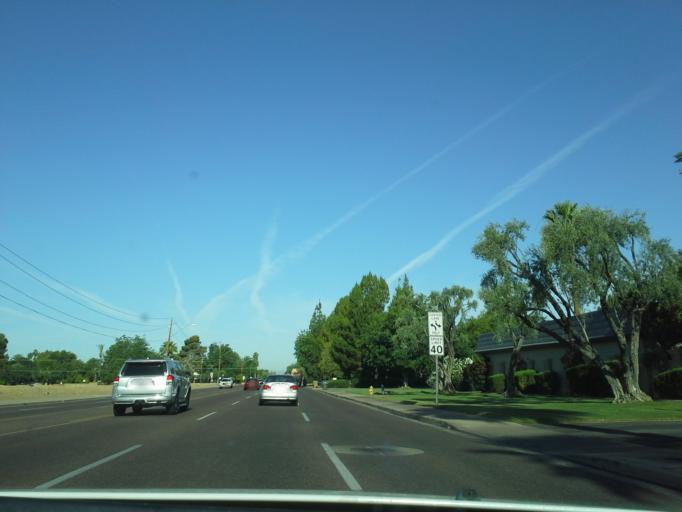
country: US
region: Arizona
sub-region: Maricopa County
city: Phoenix
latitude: 33.5529
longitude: -112.0755
